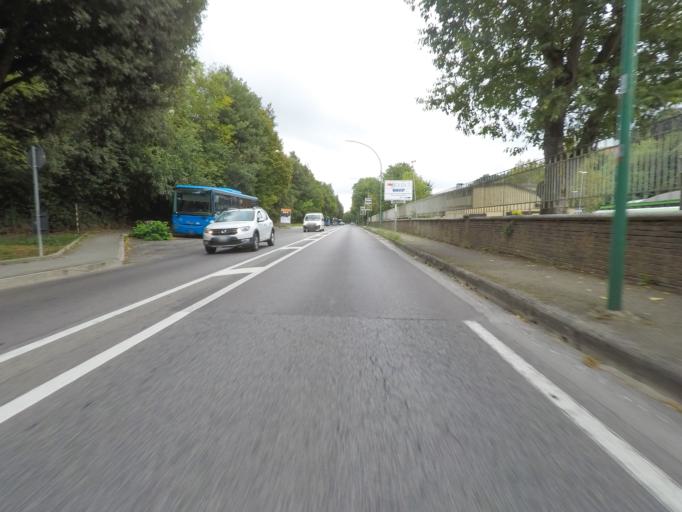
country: IT
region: Tuscany
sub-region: Provincia di Siena
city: Siena
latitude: 43.3259
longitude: 11.3423
